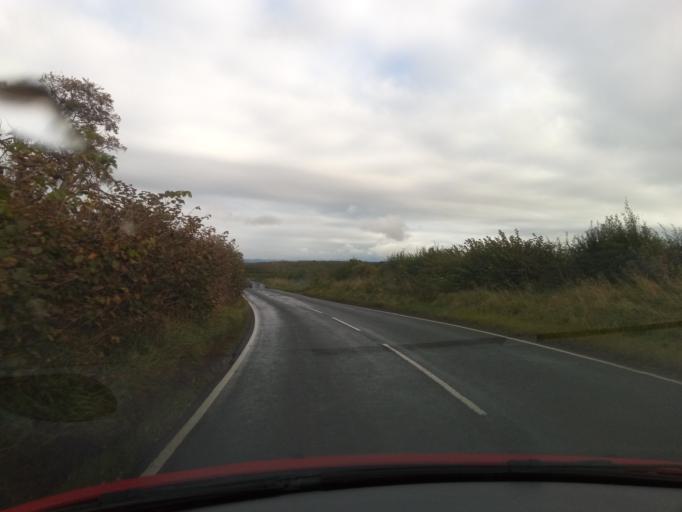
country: GB
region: Scotland
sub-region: The Scottish Borders
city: Newtown St Boswells
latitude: 55.5642
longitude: -2.6793
